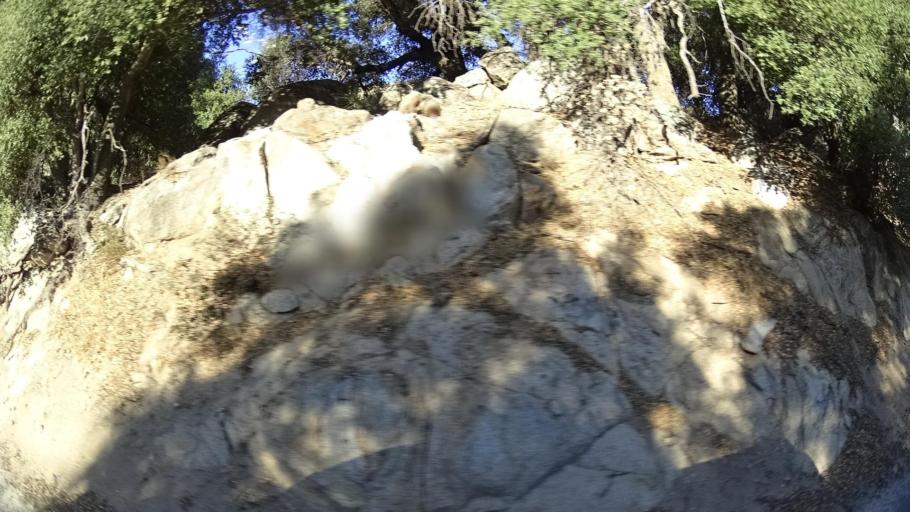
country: US
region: California
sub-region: San Diego County
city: Campo
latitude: 32.6103
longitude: -116.4742
